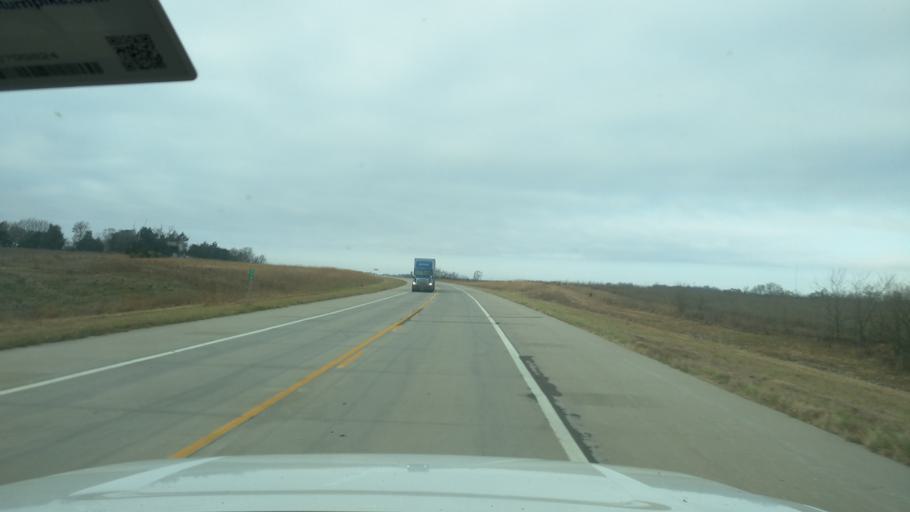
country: US
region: Kansas
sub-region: Elk County
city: Howard
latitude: 37.6372
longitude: -96.2378
